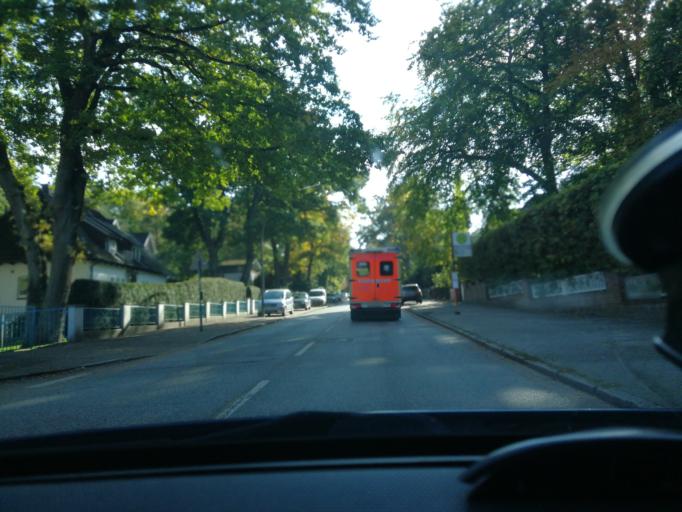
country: DE
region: Hamburg
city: Harburg
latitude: 53.4705
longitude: 9.9458
